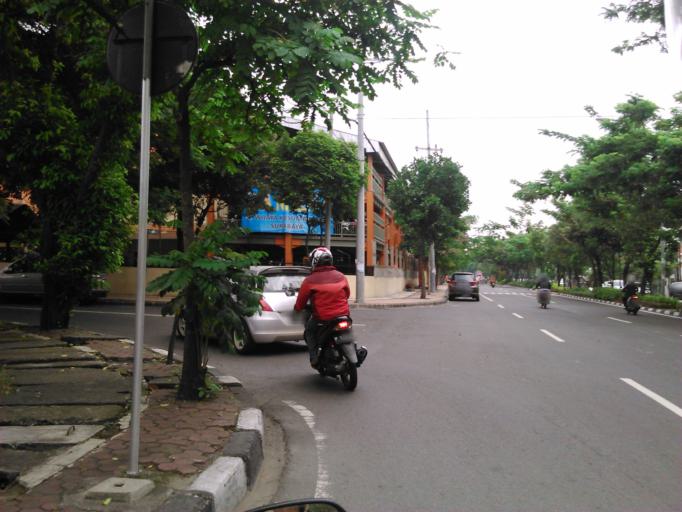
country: ID
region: East Java
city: Pacarkeling
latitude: -7.2582
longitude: 112.7508
